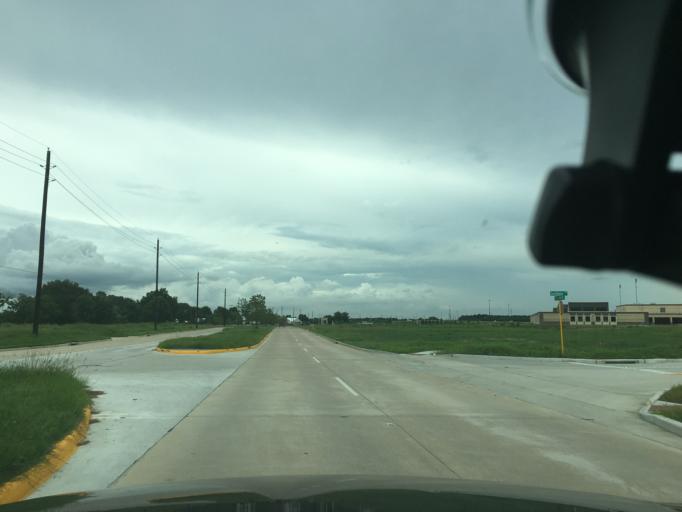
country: US
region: Texas
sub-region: Harris County
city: Tomball
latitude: 30.0622
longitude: -95.6992
